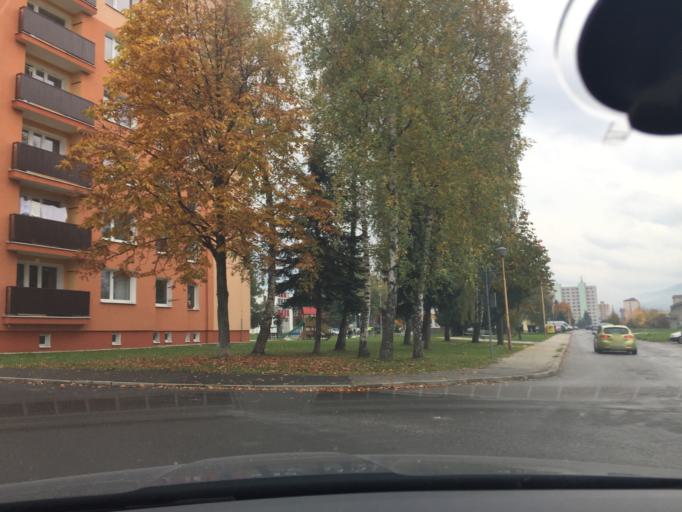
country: SK
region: Zilinsky
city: Ruzomberok
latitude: 49.0765
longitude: 19.3138
